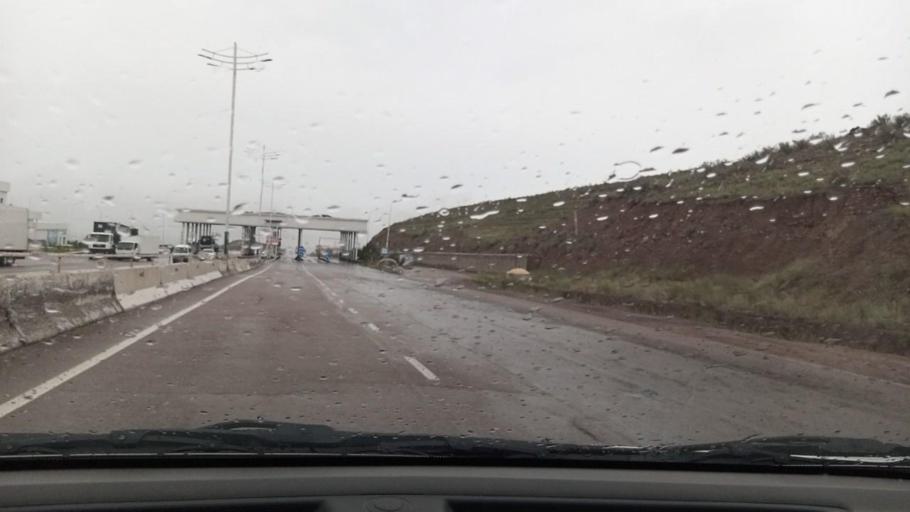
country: UZ
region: Namangan
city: Pop Shahri
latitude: 40.9230
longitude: 70.7325
